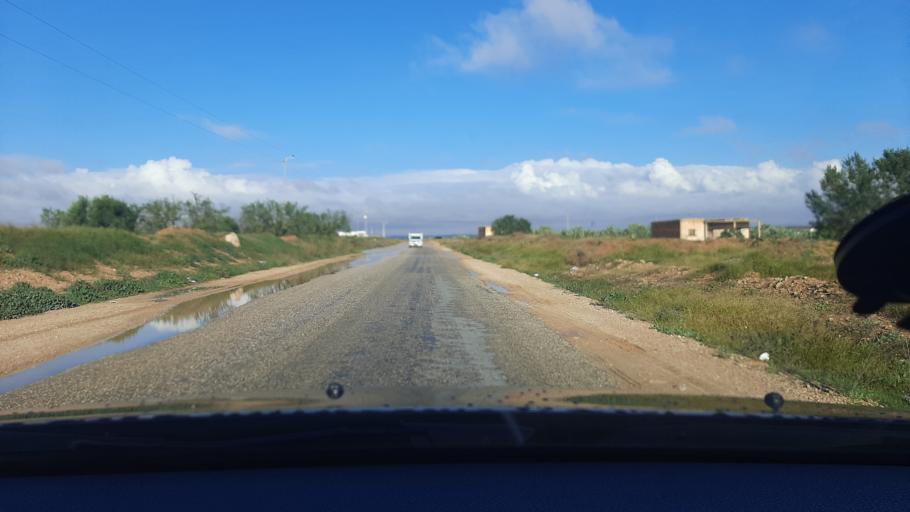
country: TN
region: Safaqis
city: Sfax
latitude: 34.8795
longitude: 10.6335
